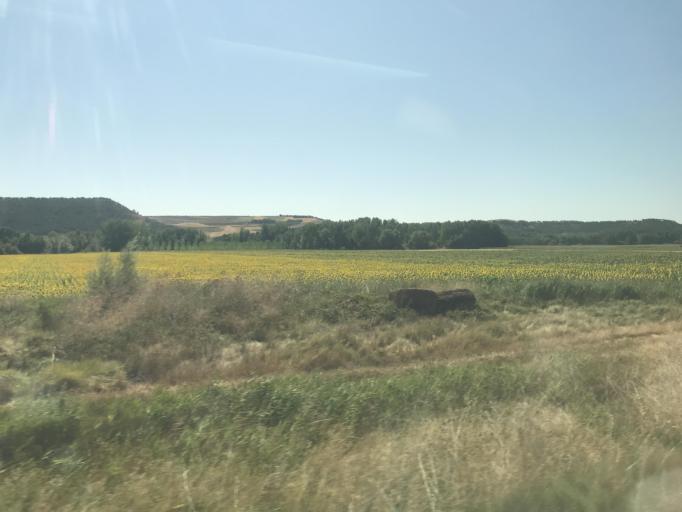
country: ES
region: Castille and Leon
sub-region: Provincia de Burgos
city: Villaldemiro
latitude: 42.2325
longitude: -3.9812
